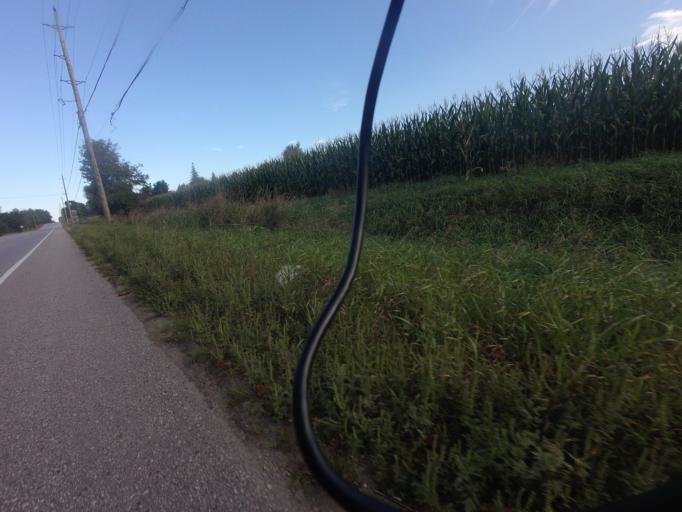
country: CA
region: Ontario
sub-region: Wellington County
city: Guelph
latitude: 43.5720
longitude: -80.3247
